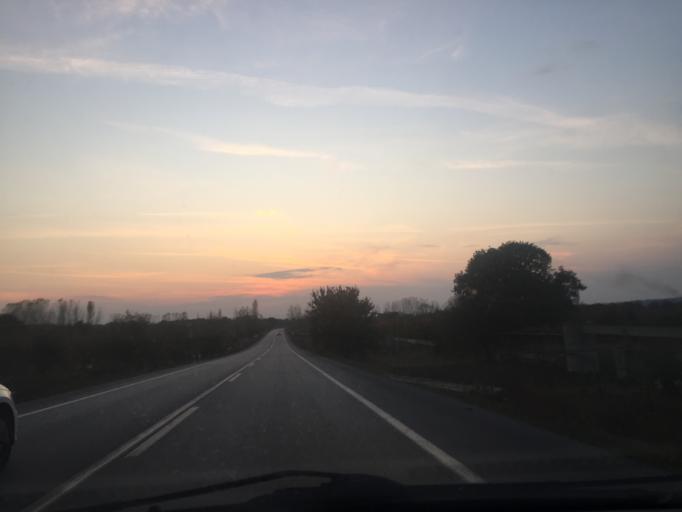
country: TR
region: Canakkale
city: Bayramic
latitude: 39.8131
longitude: 26.5684
